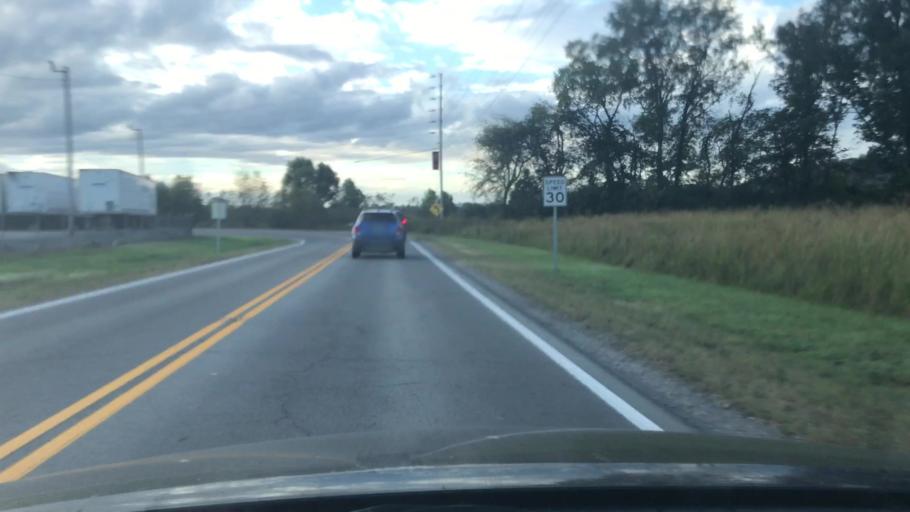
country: US
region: Tennessee
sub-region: Cheatham County
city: Ashland City
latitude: 36.2639
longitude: -87.0663
